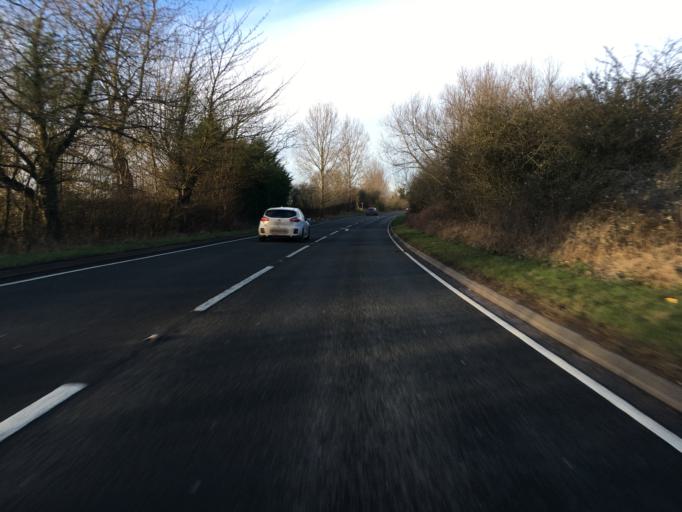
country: GB
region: England
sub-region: Warwickshire
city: Stratford-upon-Avon
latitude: 52.2270
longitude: -1.7396
